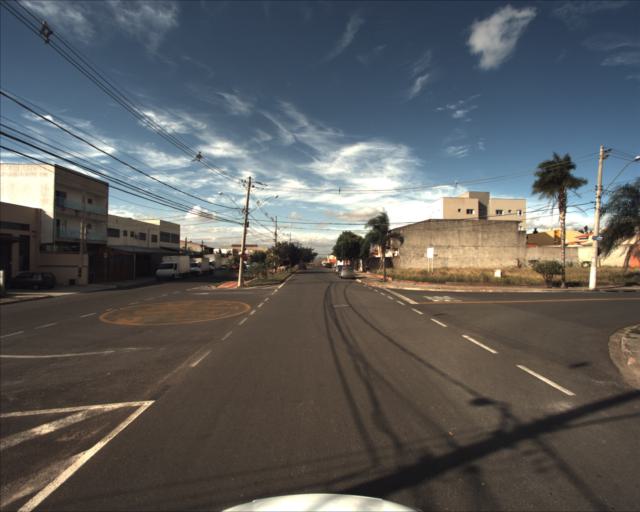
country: BR
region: Sao Paulo
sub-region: Sorocaba
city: Sorocaba
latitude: -23.5126
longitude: -47.5183
